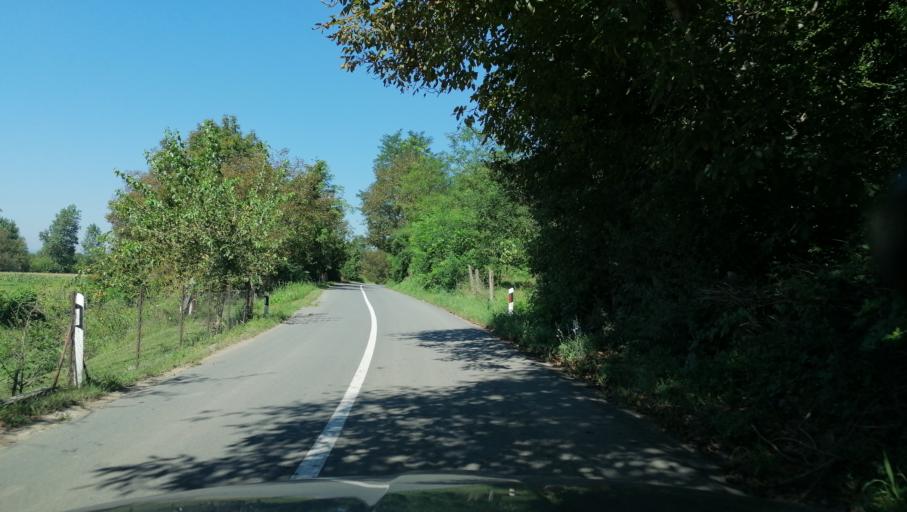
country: RS
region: Central Serbia
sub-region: Raski Okrug
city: Vrnjacka Banja
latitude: 43.6604
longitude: 20.9291
